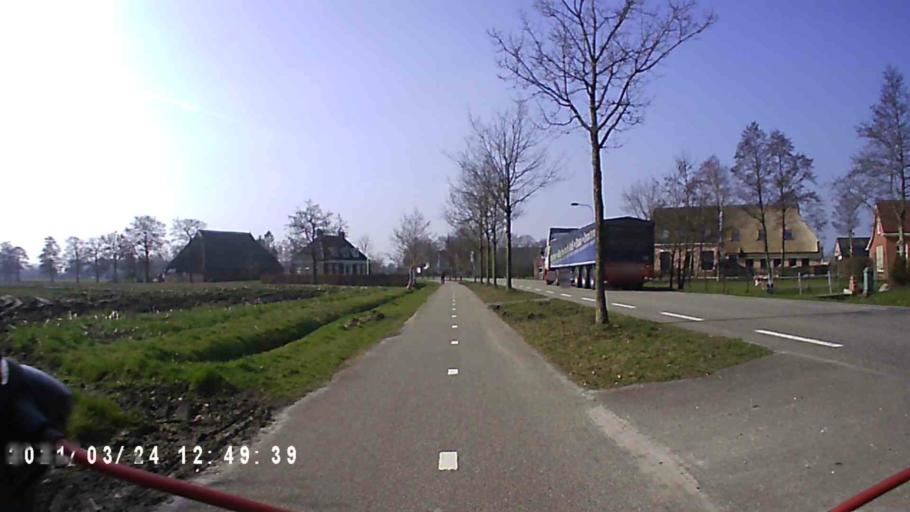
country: NL
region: Groningen
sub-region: Gemeente Leek
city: Leek
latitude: 53.1645
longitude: 6.3317
